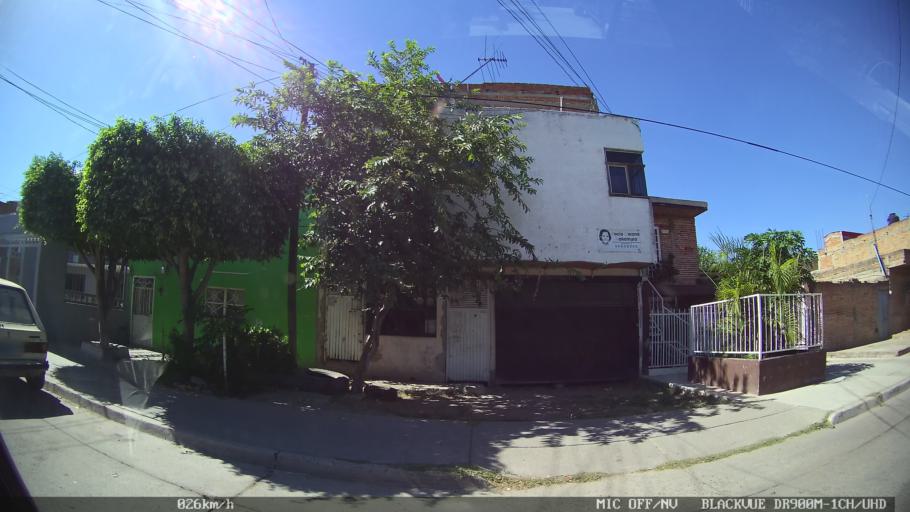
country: MX
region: Jalisco
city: Tlaquepaque
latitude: 20.6592
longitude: -103.2836
